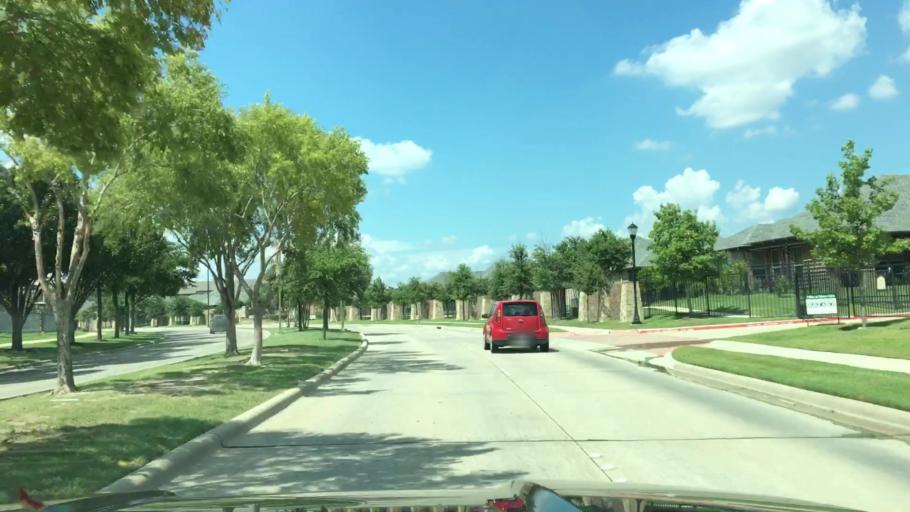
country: US
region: Texas
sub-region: Tarrant County
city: Keller
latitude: 32.9375
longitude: -97.2404
